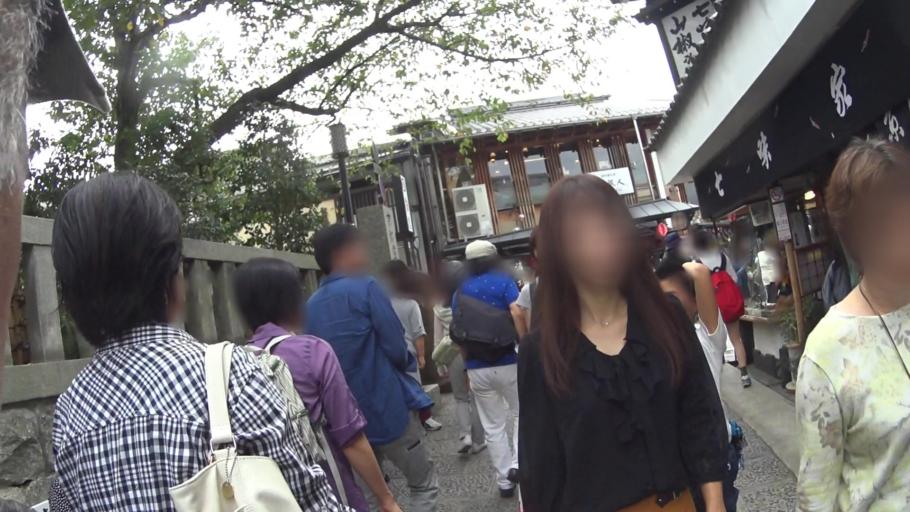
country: JP
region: Kyoto
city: Kyoto
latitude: 34.9963
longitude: 135.7809
